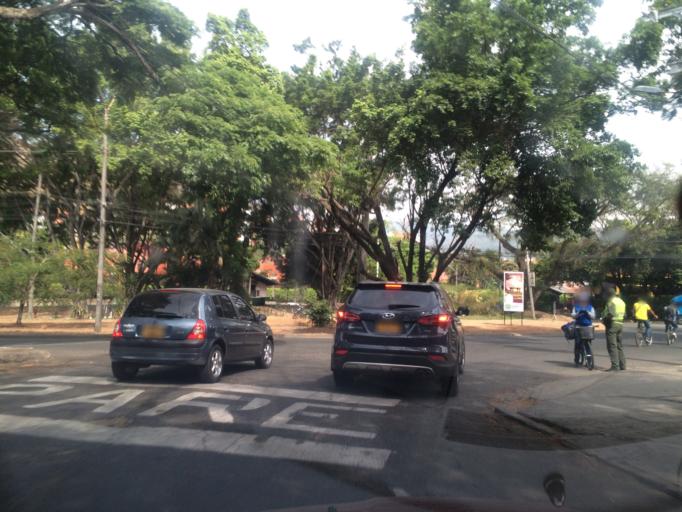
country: CO
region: Valle del Cauca
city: Cali
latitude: 3.4099
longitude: -76.5553
